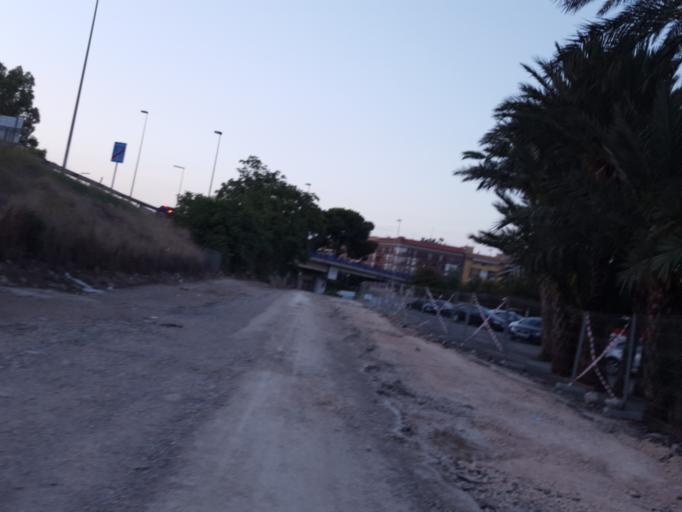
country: ES
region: Murcia
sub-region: Murcia
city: Murcia
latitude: 37.9807
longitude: -1.1380
